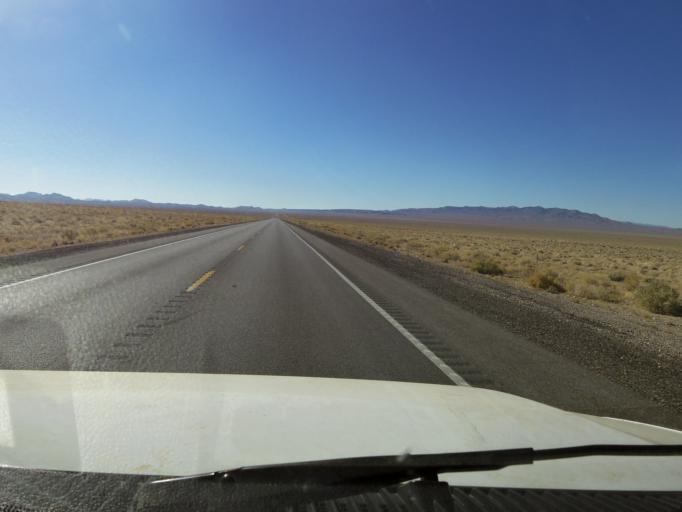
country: US
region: Nevada
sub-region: Nye County
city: Tonopah
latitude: 37.8911
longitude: -117.2428
